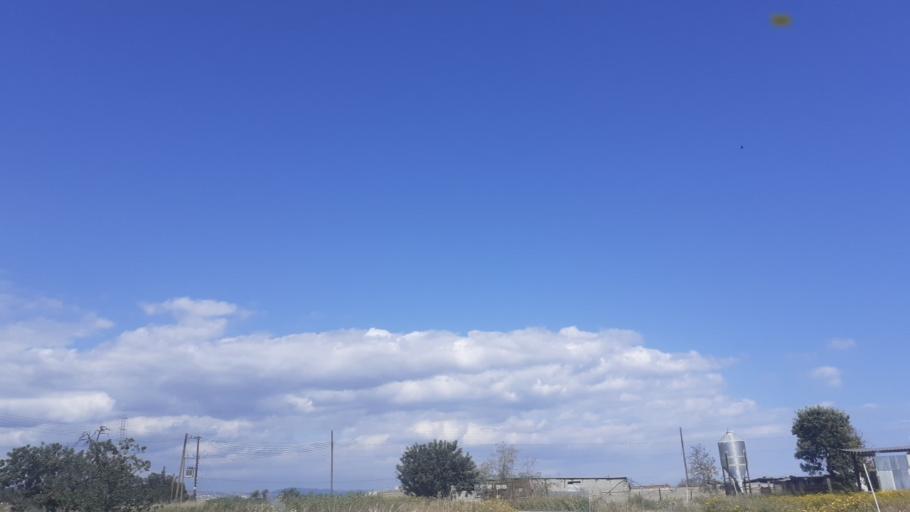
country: CY
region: Limassol
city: Ypsonas
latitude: 34.6745
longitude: 32.9805
